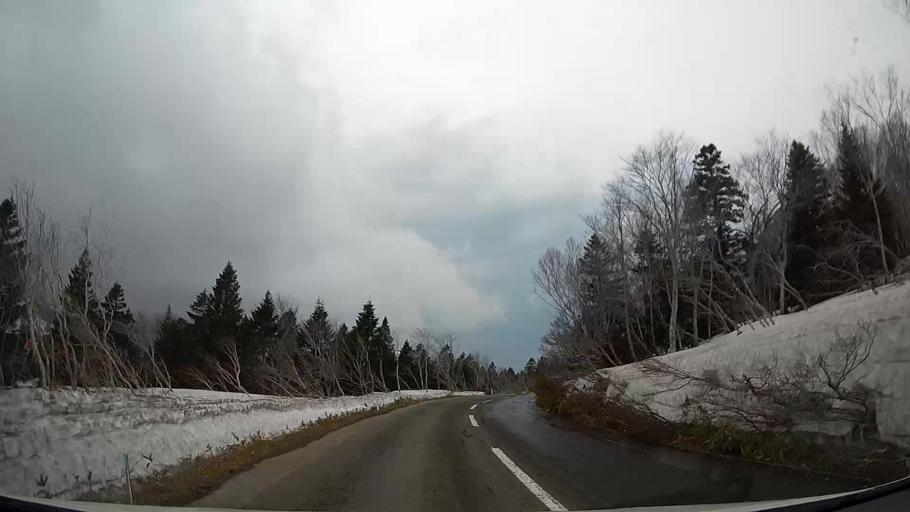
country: JP
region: Aomori
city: Aomori Shi
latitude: 40.6363
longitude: 140.8701
